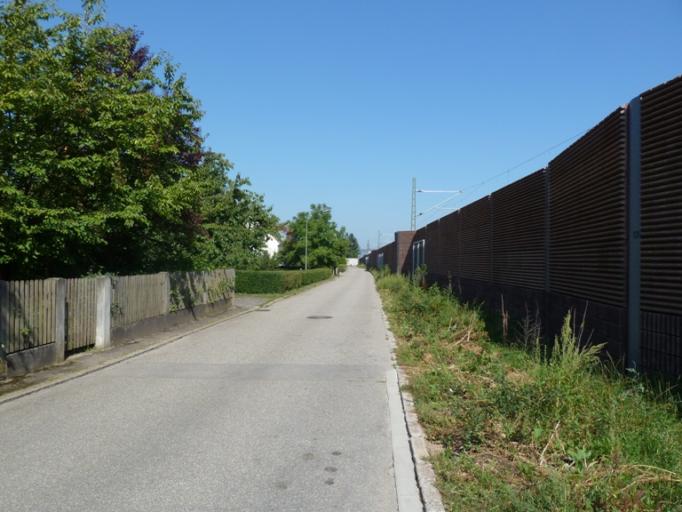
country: DE
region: Baden-Wuerttemberg
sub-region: Freiburg Region
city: Eimeldingen
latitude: 47.6285
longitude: 7.5949
